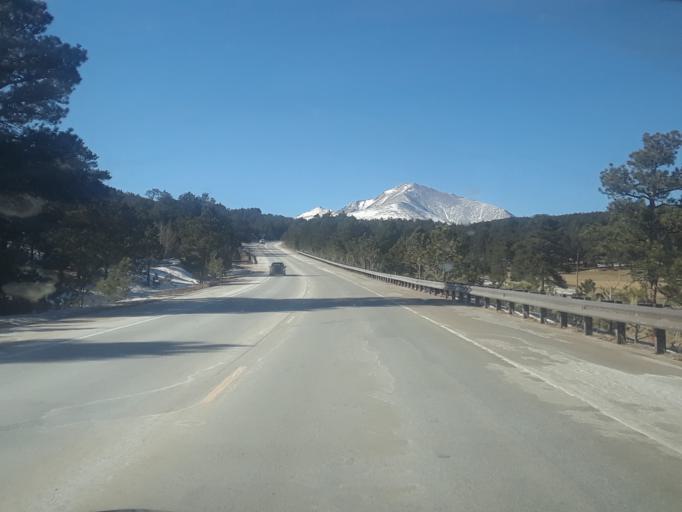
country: US
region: Colorado
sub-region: Larimer County
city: Estes Park
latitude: 40.1826
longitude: -105.4762
